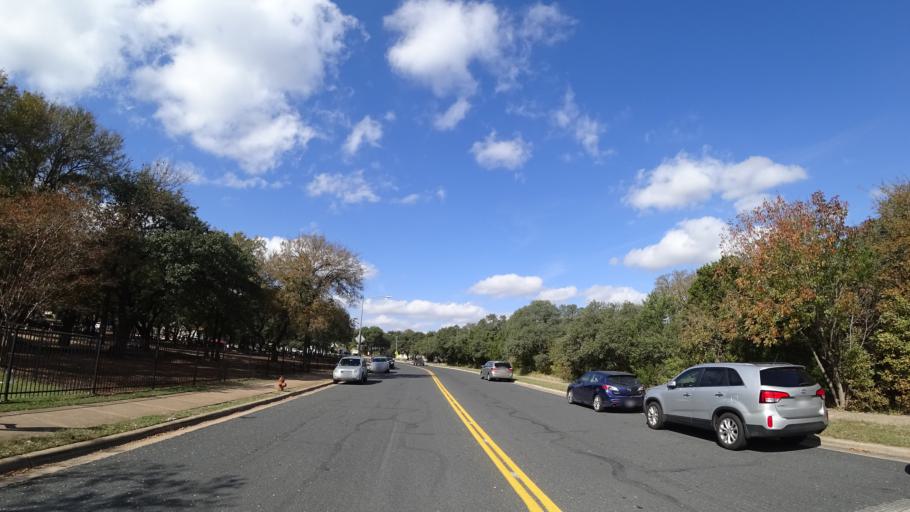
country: US
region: Texas
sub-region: Travis County
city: Wells Branch
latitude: 30.4227
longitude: -97.7174
